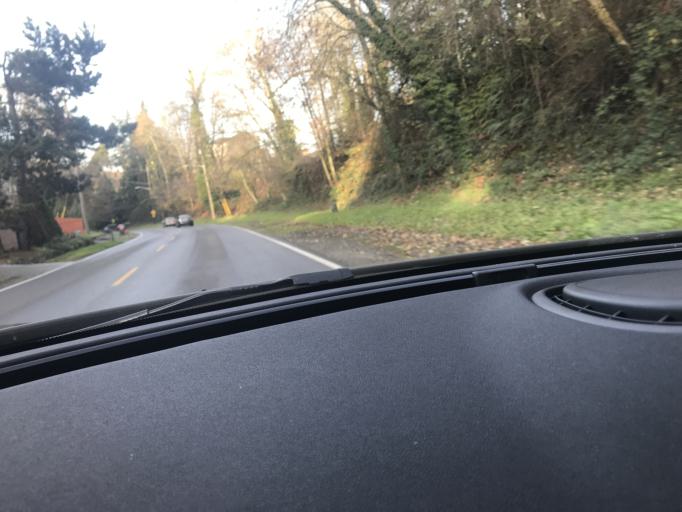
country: US
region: Washington
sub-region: King County
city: White Center
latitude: 47.5358
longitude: -122.3576
